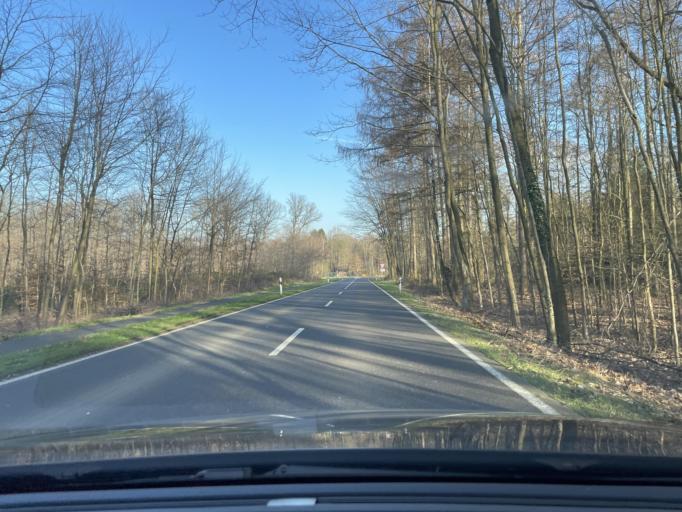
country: DE
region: North Rhine-Westphalia
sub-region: Regierungsbezirk Dusseldorf
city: Bruggen
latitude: 51.2331
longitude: 6.1836
